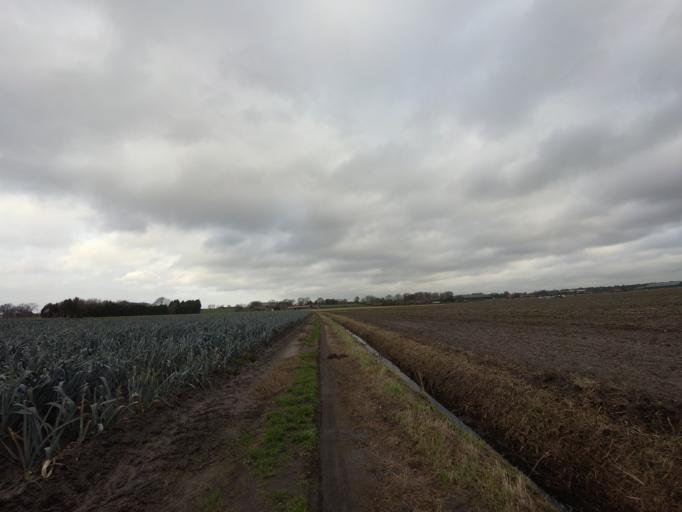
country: NL
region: North Brabant
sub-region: Gemeente Woensdrecht
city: Woensdrecht
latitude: 51.3795
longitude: 4.3336
